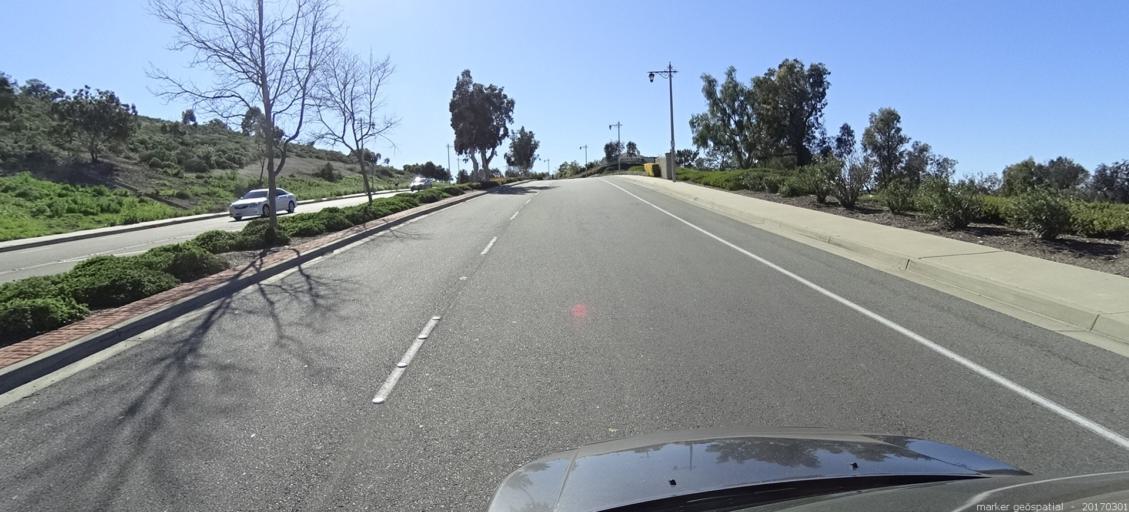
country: US
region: California
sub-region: Orange County
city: Villa Park
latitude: 33.8370
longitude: -117.7931
